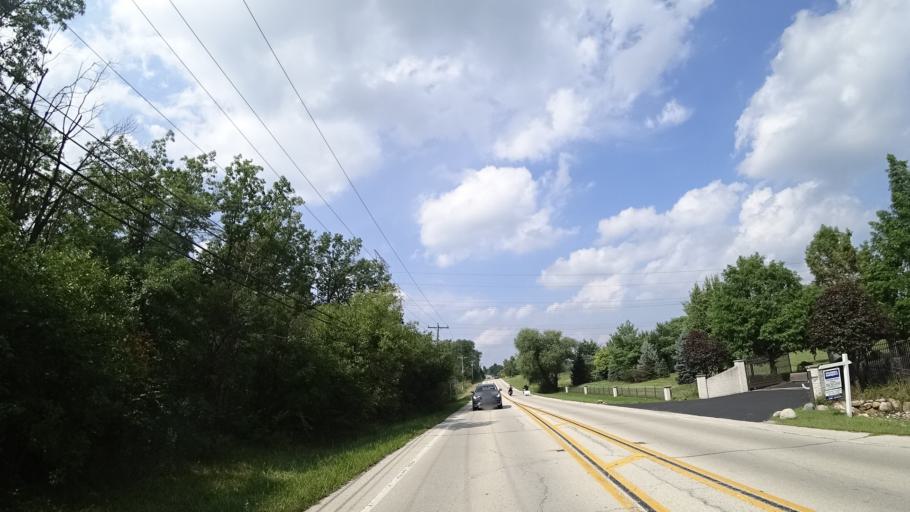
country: US
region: Illinois
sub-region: Will County
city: Goodings Grove
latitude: 41.6528
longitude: -87.8929
